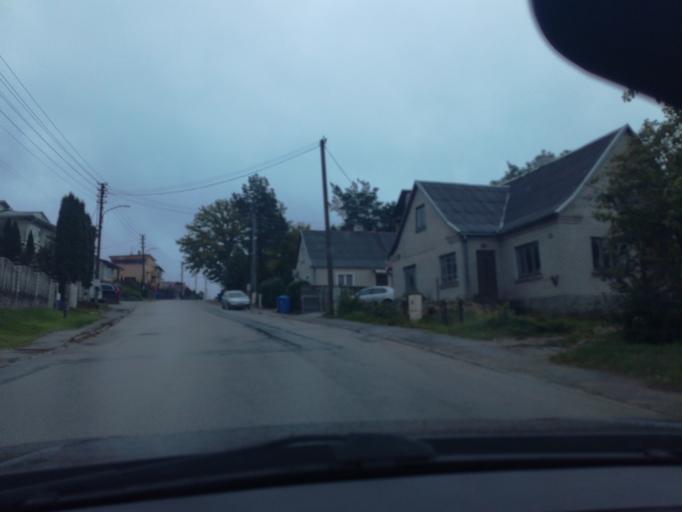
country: LT
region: Alytaus apskritis
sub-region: Alytus
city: Alytus
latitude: 54.4006
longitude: 24.0710
